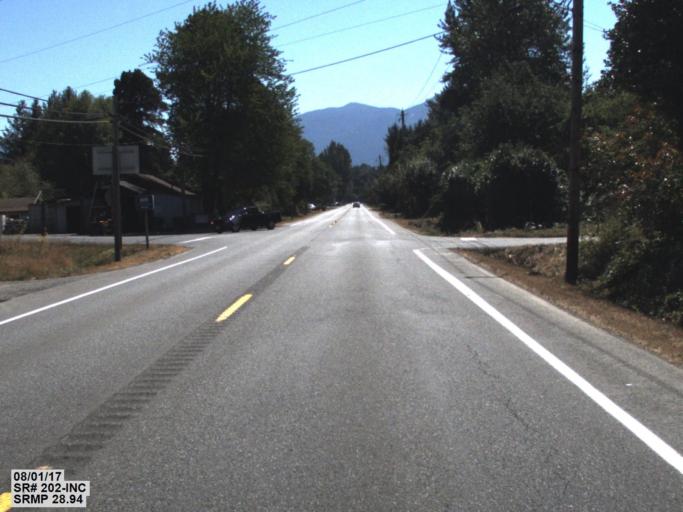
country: US
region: Washington
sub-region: King County
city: North Bend
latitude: 47.5056
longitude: -121.7978
